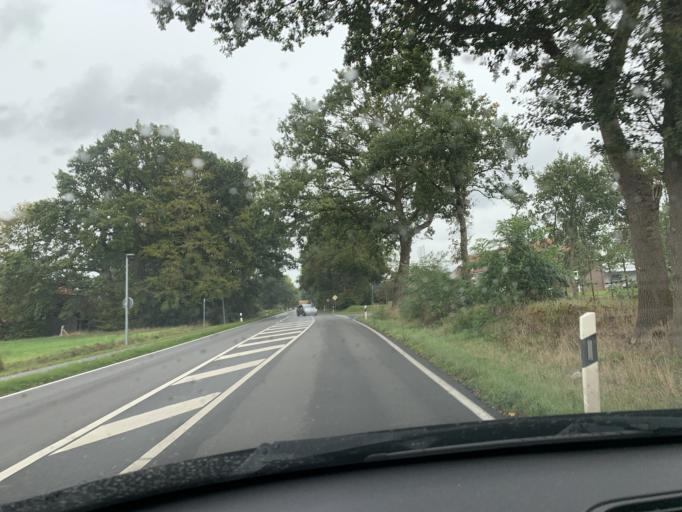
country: DE
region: Lower Saxony
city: Bad Zwischenahn
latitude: 53.1793
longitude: 8.0686
